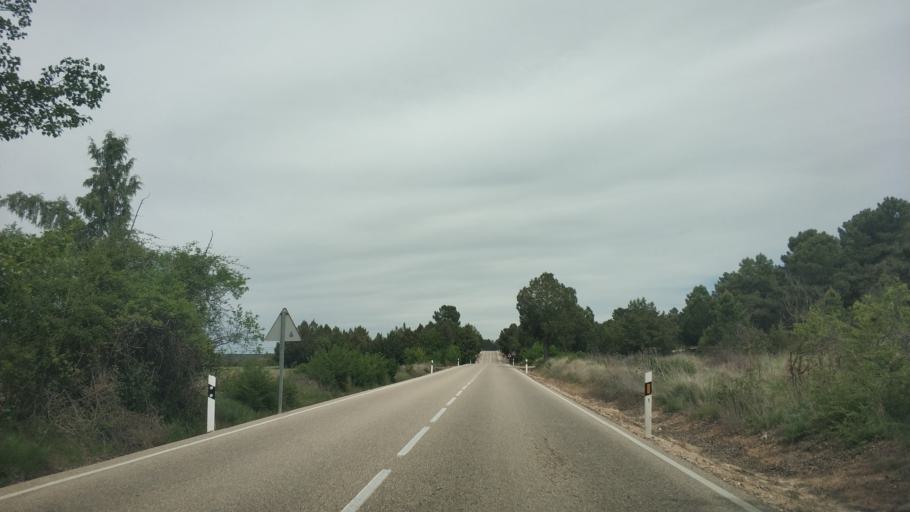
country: ES
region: Castille and Leon
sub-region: Provincia de Soria
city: Valdenebro
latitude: 41.5644
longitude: -2.9911
